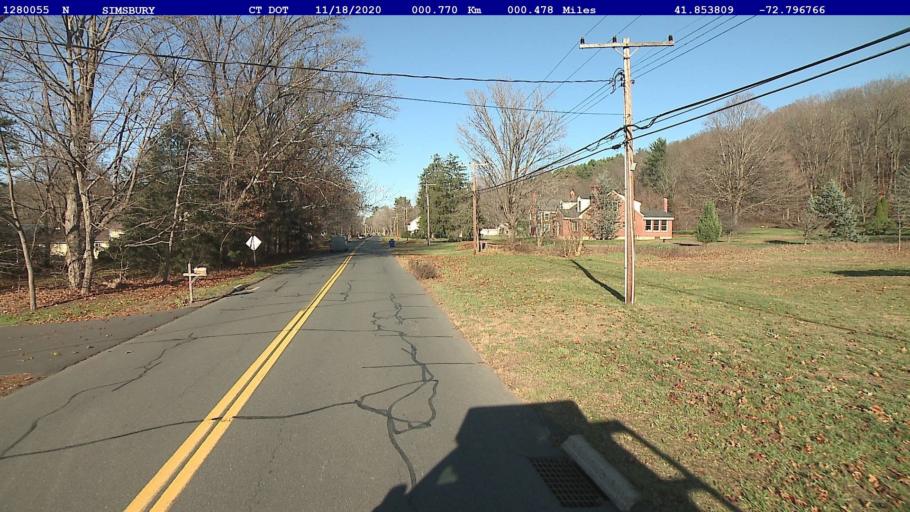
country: US
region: Connecticut
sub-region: Hartford County
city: Simsbury Center
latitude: 41.8538
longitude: -72.7968
